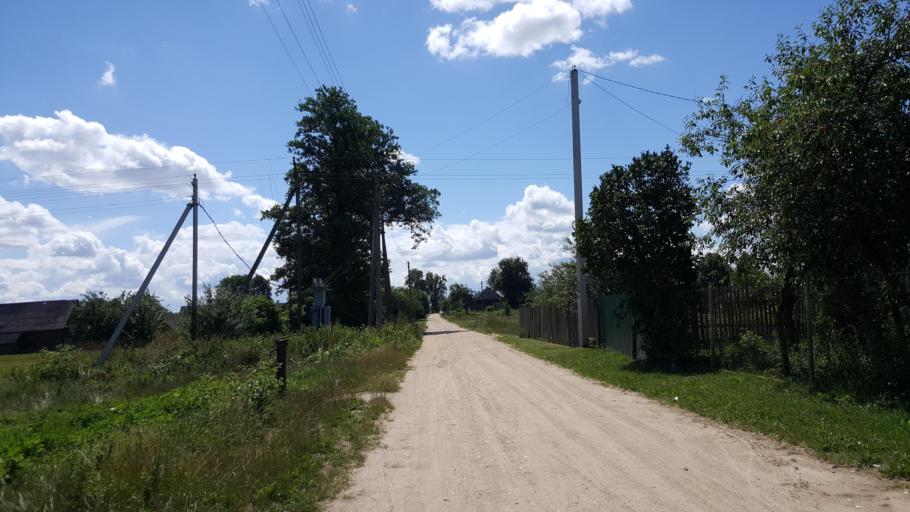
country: BY
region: Brest
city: Kamyanyets
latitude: 52.3300
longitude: 23.9126
